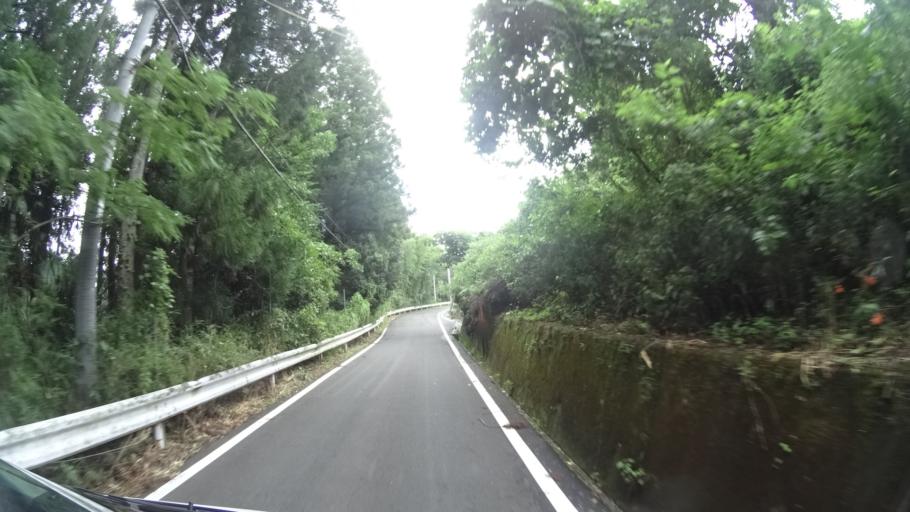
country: JP
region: Kyoto
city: Ayabe
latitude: 35.2722
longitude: 135.3475
